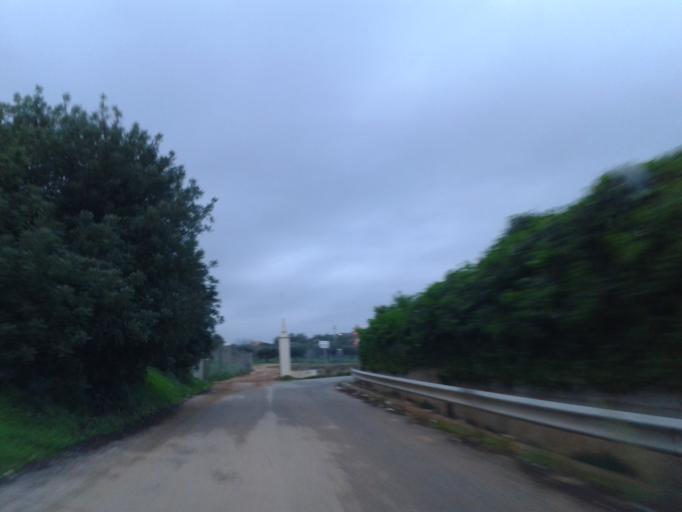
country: PT
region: Faro
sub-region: Loule
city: Boliqueime
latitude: 37.1235
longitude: -8.1540
